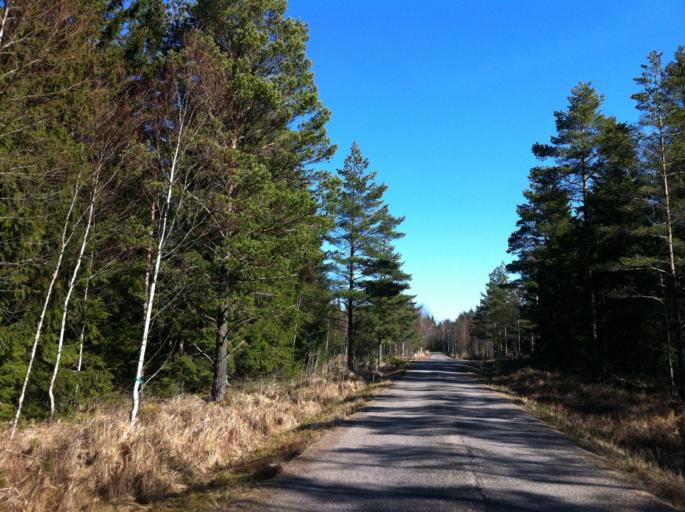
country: SE
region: Vaestra Goetaland
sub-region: Vanersborgs Kommun
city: Vargon
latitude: 58.3883
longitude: 12.4554
